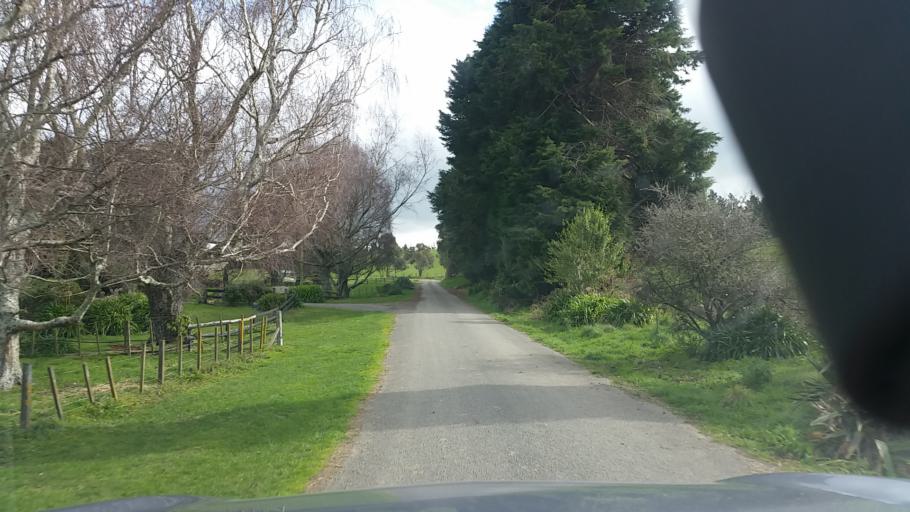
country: NZ
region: Hawke's Bay
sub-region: Napier City
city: Napier
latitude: -39.2049
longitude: 176.9300
